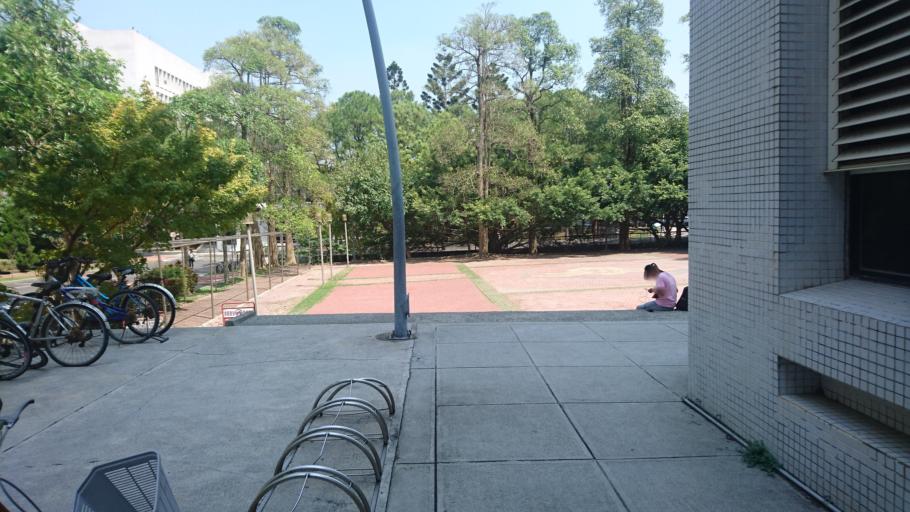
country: TW
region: Taiwan
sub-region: Hsinchu
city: Hsinchu
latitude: 24.7939
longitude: 120.9920
